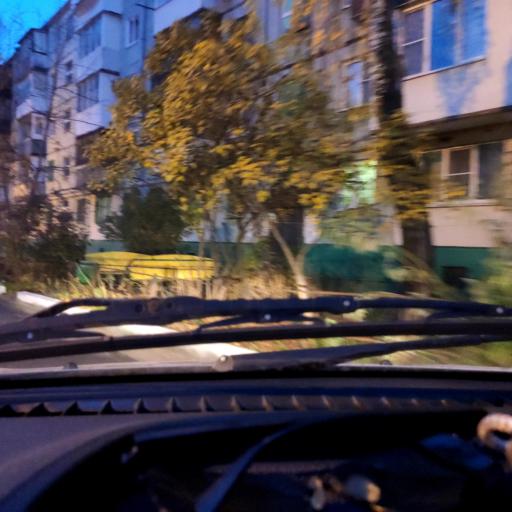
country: RU
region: Samara
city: Tol'yatti
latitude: 53.5130
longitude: 49.4372
